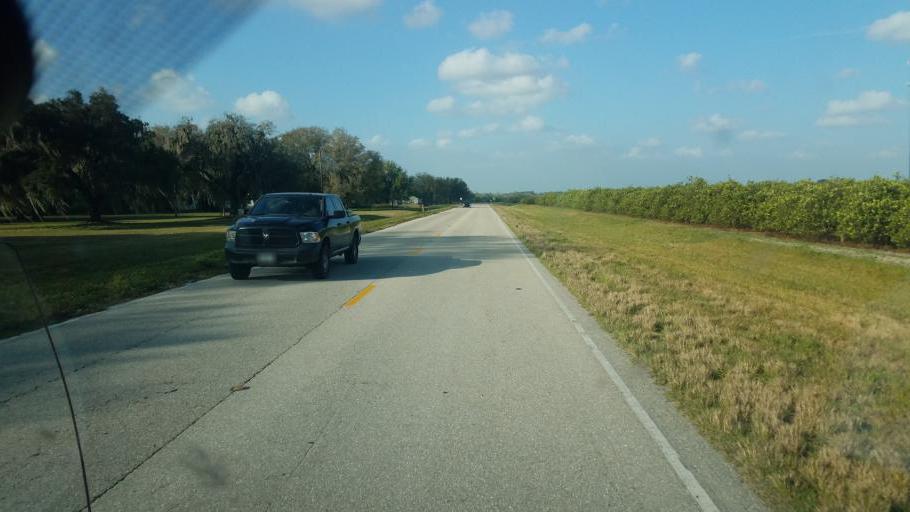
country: US
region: Florida
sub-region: Hardee County
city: Bowling Green
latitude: 27.5886
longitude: -81.9363
